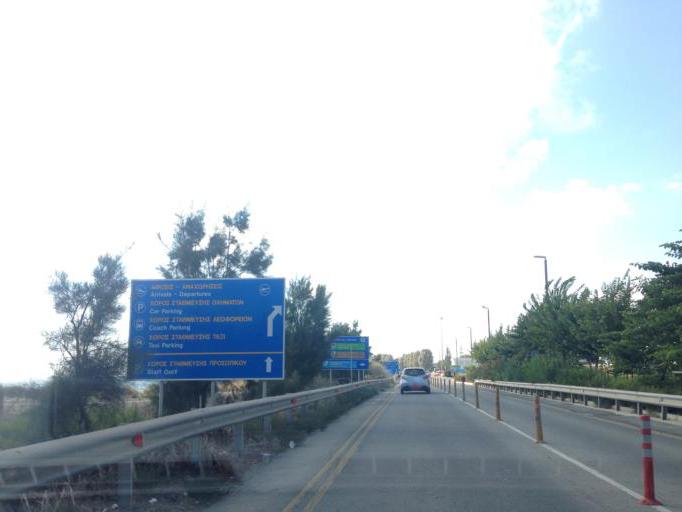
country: CY
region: Pafos
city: Paphos
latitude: 34.7098
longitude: 32.4894
